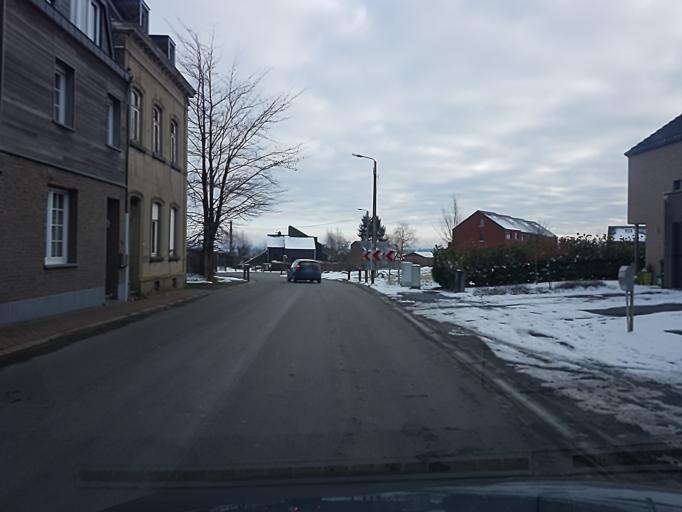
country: BE
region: Wallonia
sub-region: Province de Liege
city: Soumagne
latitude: 50.6306
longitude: 5.7633
